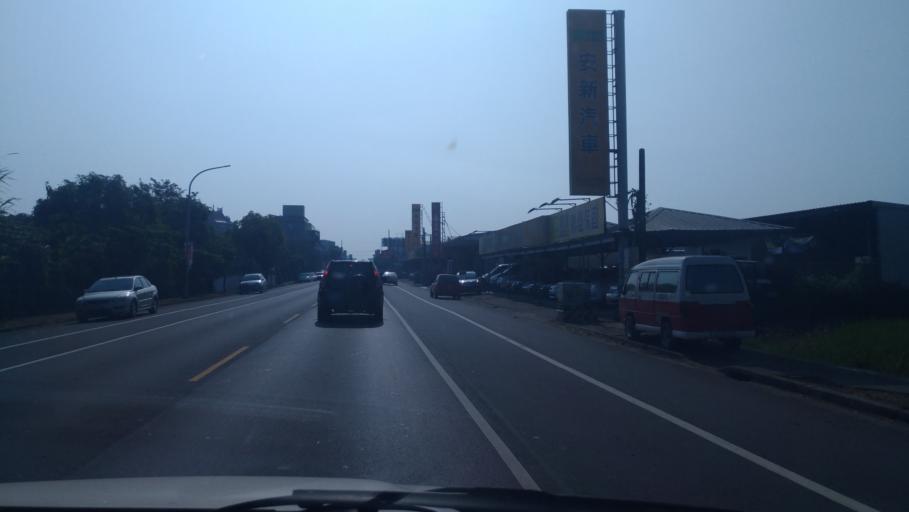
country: TW
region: Taiwan
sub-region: Chiayi
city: Jiayi Shi
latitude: 23.5056
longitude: 120.4375
